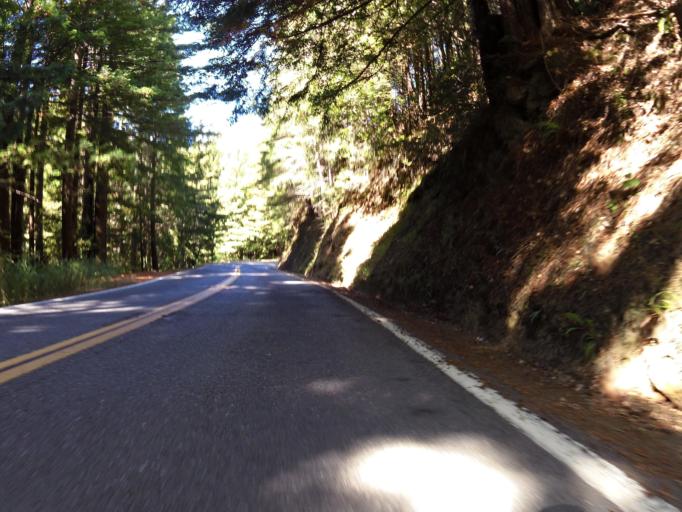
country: US
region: California
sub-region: Humboldt County
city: Redway
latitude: 39.7962
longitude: -123.8169
